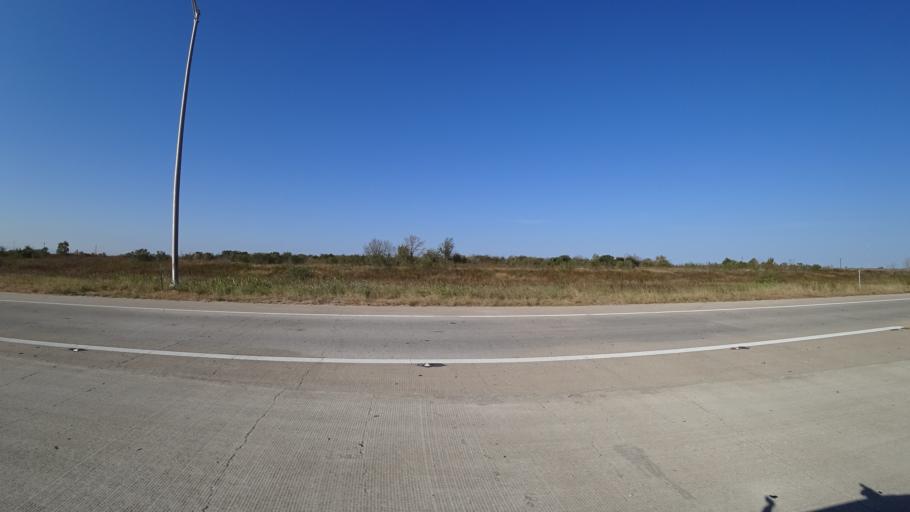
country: US
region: Texas
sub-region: Travis County
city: Hornsby Bend
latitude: 30.2234
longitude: -97.6229
